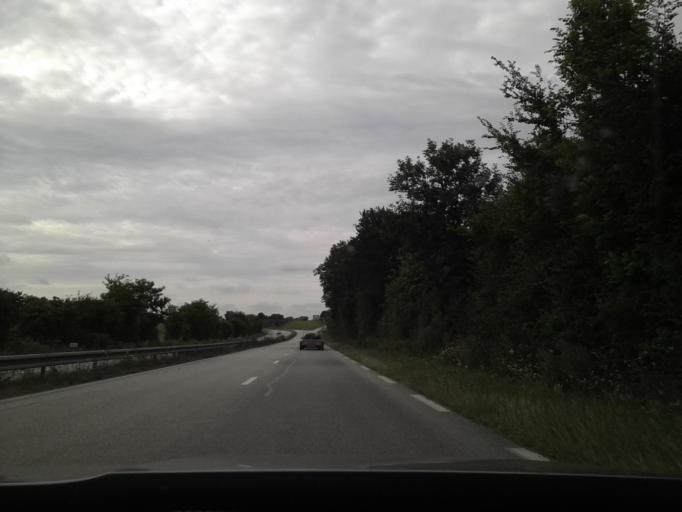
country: FR
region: Lower Normandy
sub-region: Departement de la Manche
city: Montebourg
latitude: 49.4695
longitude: -1.3644
